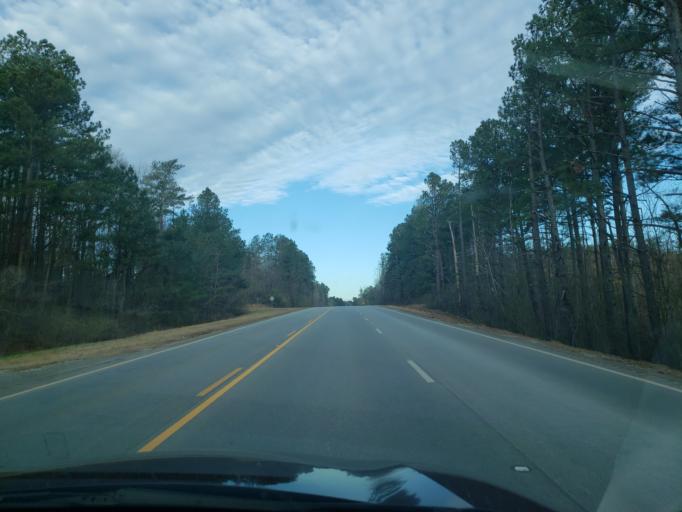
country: US
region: Alabama
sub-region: Randolph County
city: Wedowee
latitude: 33.4070
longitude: -85.5354
